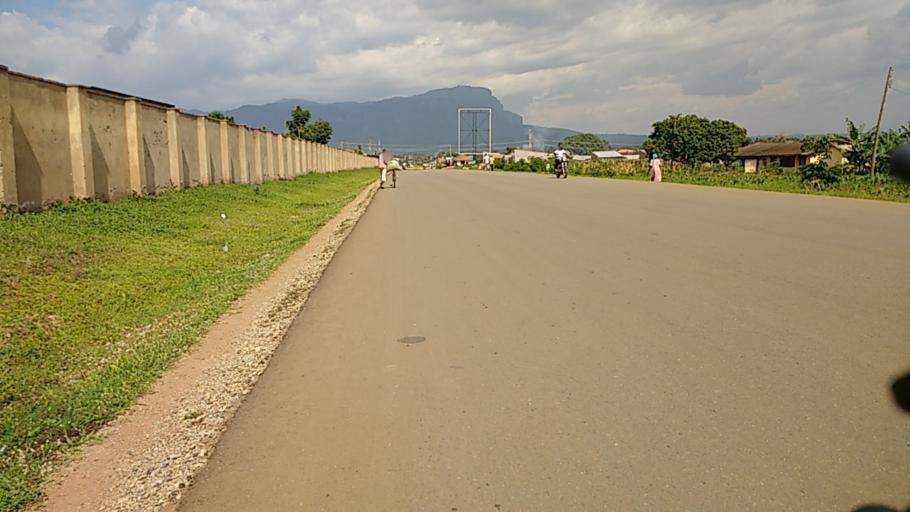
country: UG
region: Eastern Region
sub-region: Mbale District
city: Mbale
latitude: 1.0778
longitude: 34.1578
